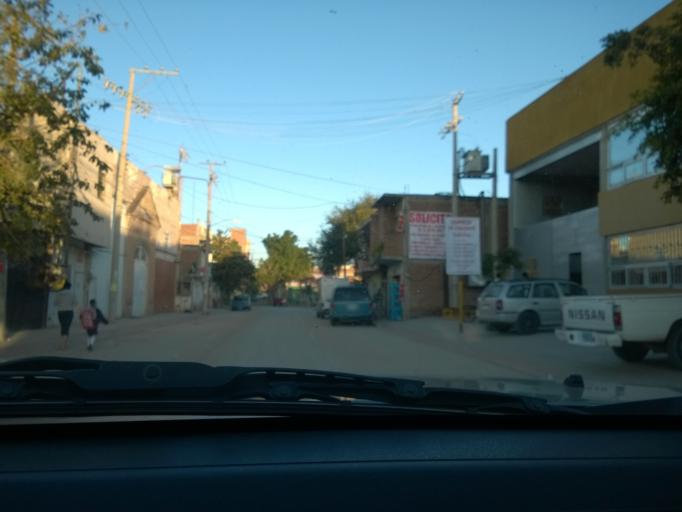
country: MX
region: Guanajuato
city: Leon
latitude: 21.1288
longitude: -101.6595
